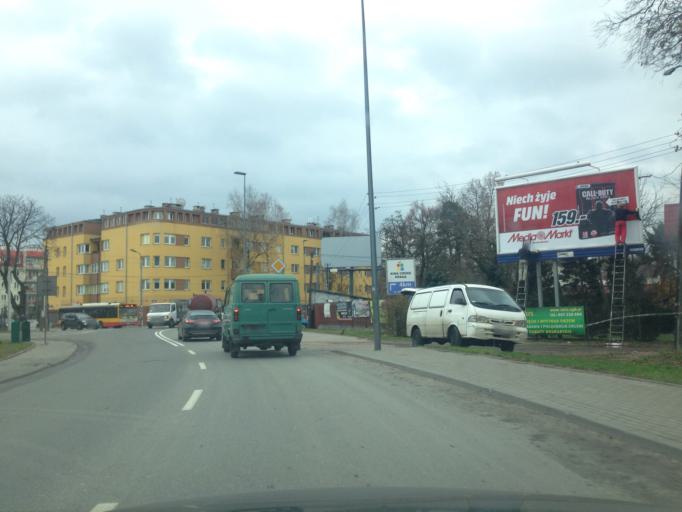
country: PL
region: Masovian Voivodeship
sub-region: Warszawa
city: Rembertow
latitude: 52.2565
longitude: 21.1564
